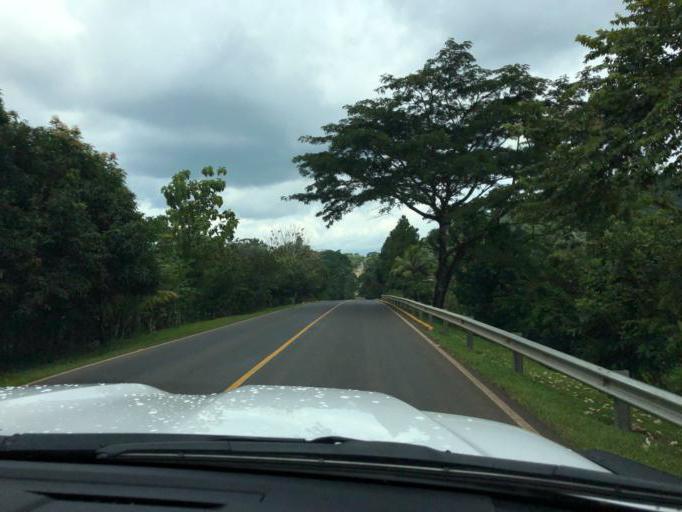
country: NI
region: Chontales
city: Villa Sandino
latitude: 11.9973
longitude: -84.8453
